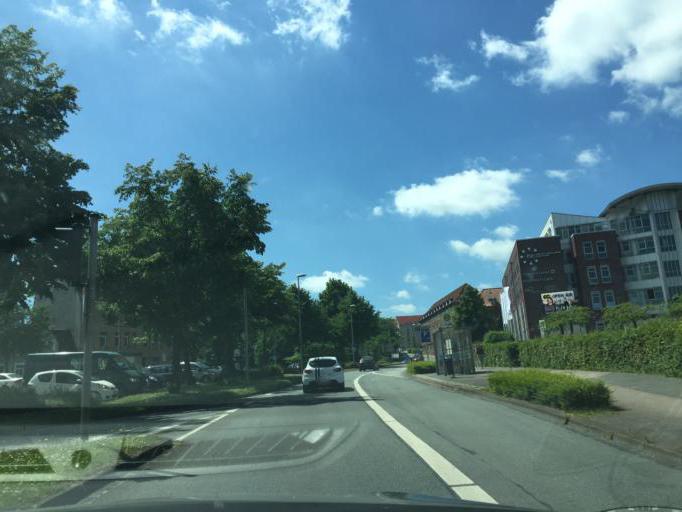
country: DE
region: Schleswig-Holstein
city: Flensburg
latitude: 54.7805
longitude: 9.4351
